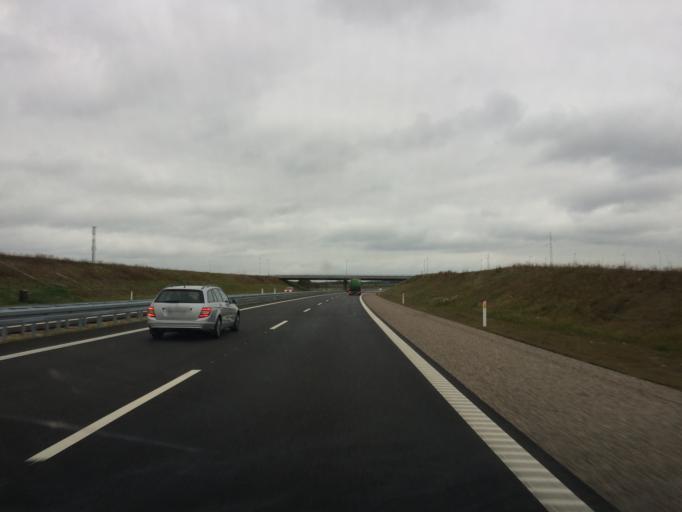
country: DK
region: Central Jutland
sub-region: Silkeborg Kommune
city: Silkeborg
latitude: 56.1542
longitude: 9.4572
